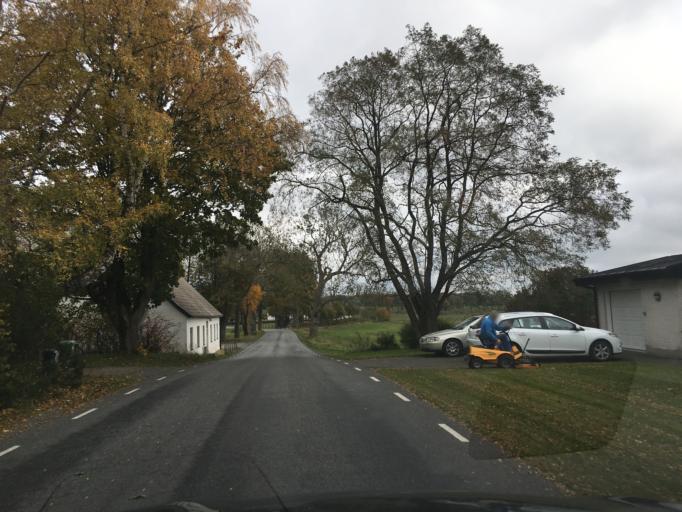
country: SE
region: Skane
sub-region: Tomelilla Kommun
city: Tomelilla
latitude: 55.6514
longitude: 14.0279
